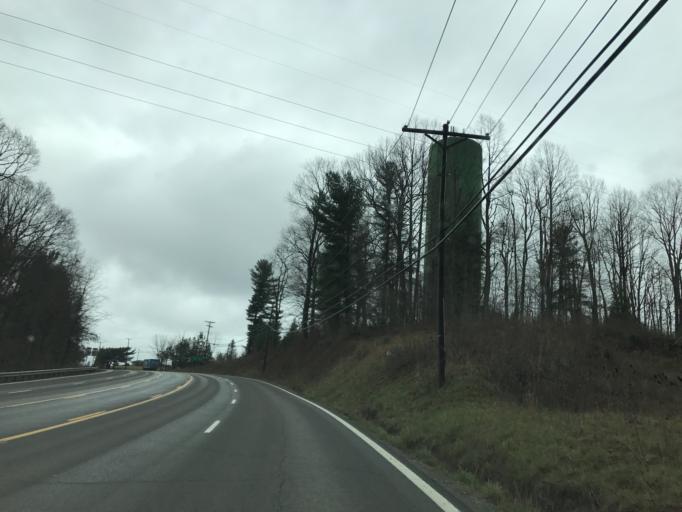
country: US
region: West Virginia
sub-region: Raleigh County
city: Prosperity
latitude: 37.8282
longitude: -81.1962
